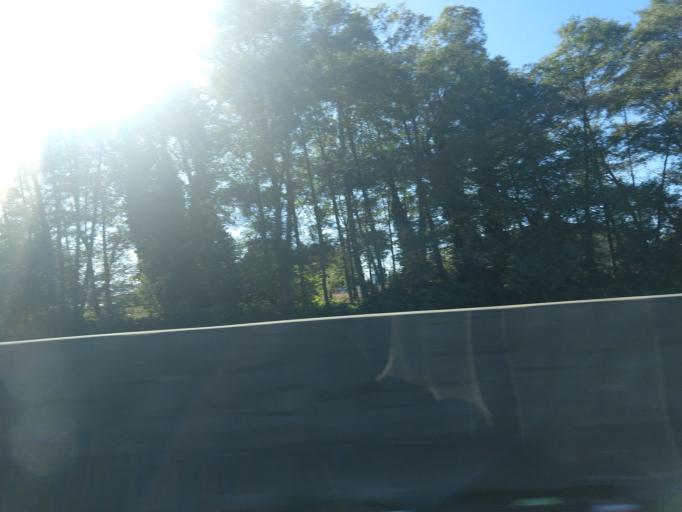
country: US
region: California
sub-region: Humboldt County
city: Fortuna
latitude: 40.5838
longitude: -124.1520
